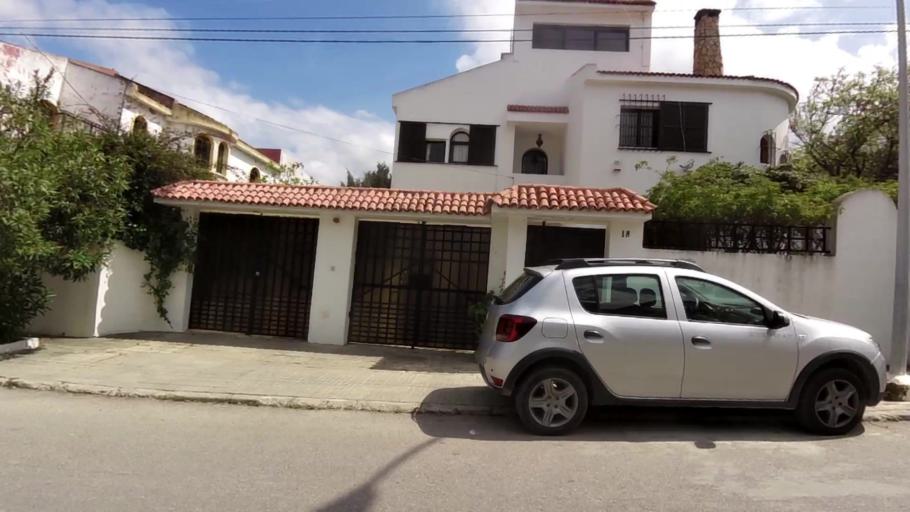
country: MA
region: Tanger-Tetouan
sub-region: Tanger-Assilah
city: Tangier
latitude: 35.7750
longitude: -5.7727
